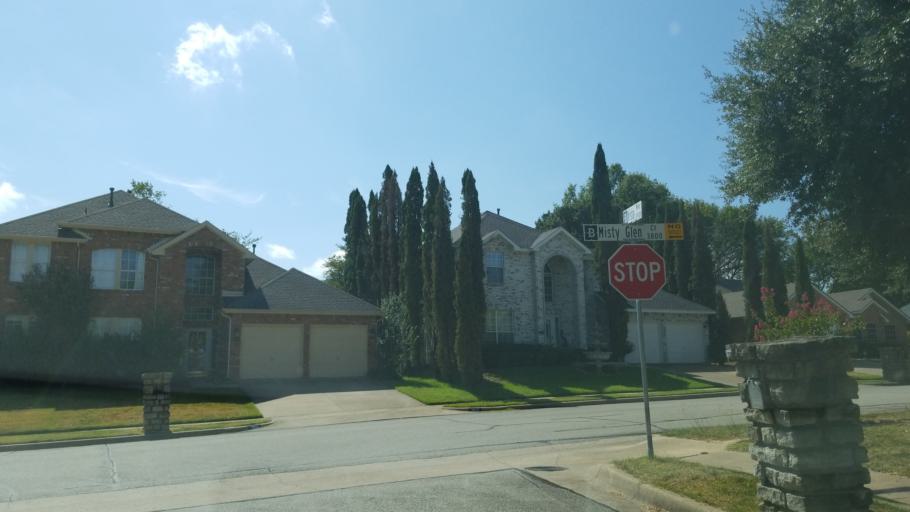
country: US
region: Texas
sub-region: Tarrant County
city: Euless
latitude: 32.8583
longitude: -97.1036
